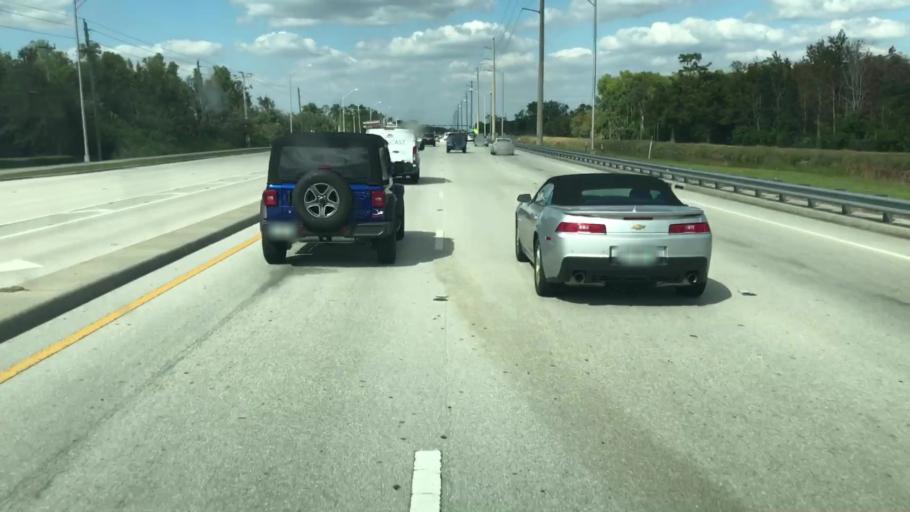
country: US
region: Florida
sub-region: Collier County
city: Vineyards
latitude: 26.2606
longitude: -81.6889
